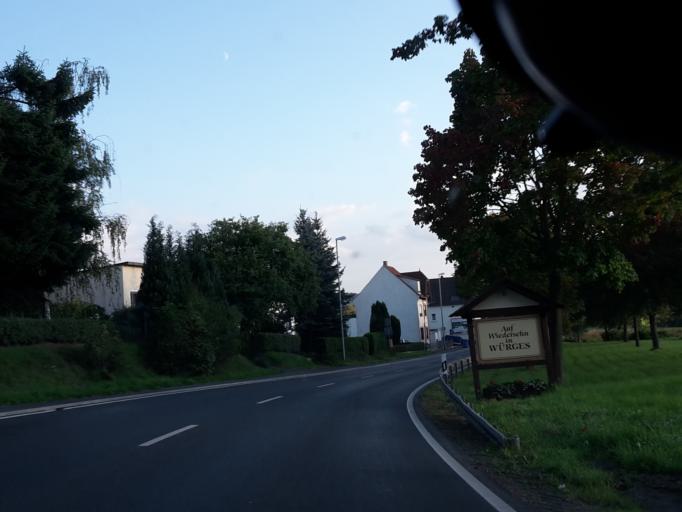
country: DE
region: Hesse
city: Bad Camberg
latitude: 50.2815
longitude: 8.2804
